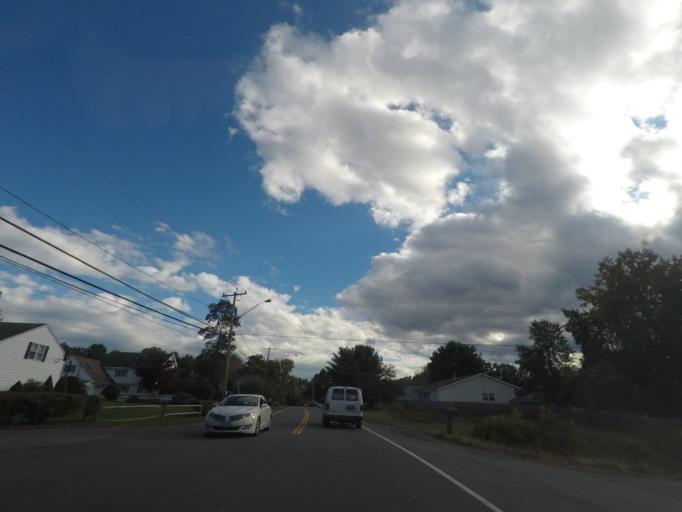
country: US
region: New York
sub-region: Schenectady County
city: Niskayuna
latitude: 42.7507
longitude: -73.8388
